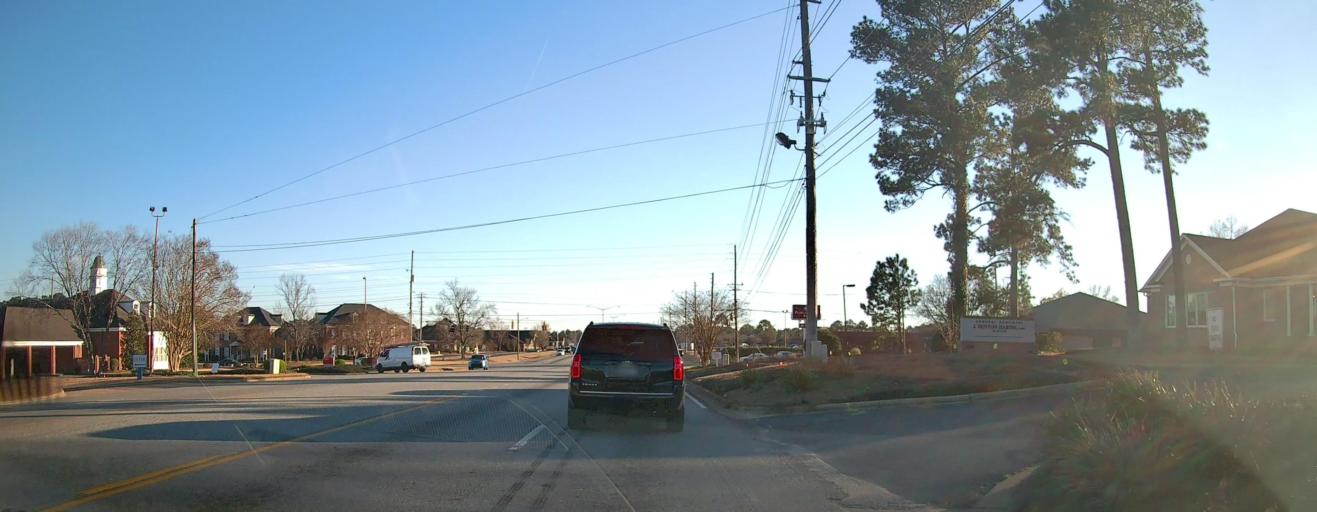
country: US
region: Georgia
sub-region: Dougherty County
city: Albany
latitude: 31.6147
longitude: -84.2231
